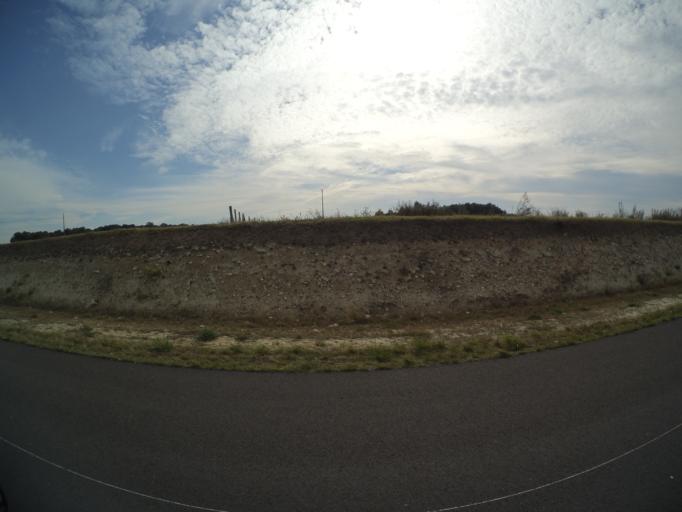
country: FR
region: Pays de la Loire
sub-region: Departement de Maine-et-Loire
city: Vaudelnay
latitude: 47.2061
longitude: -0.1974
